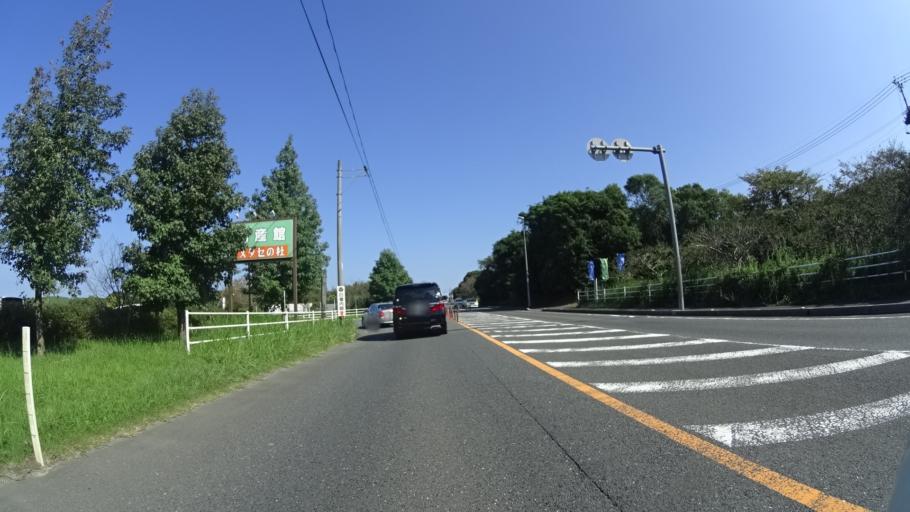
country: JP
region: Fukuoka
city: Tsuiki
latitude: 33.6743
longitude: 131.0126
